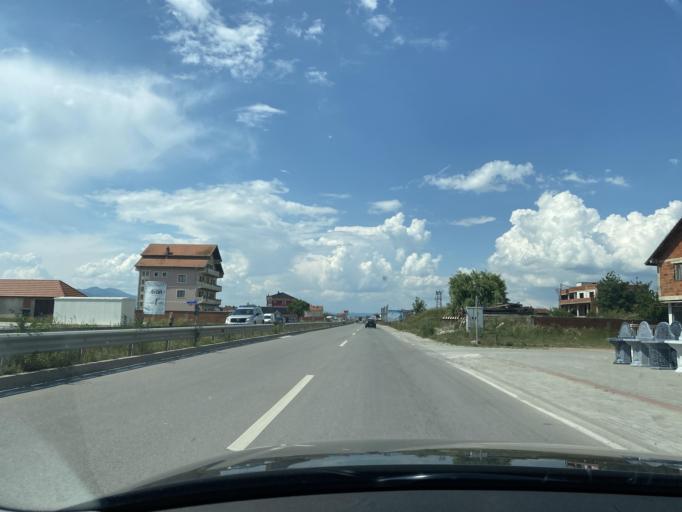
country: XK
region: Pristina
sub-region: Podujevo
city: Podujeva
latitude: 42.8700
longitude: 21.1829
